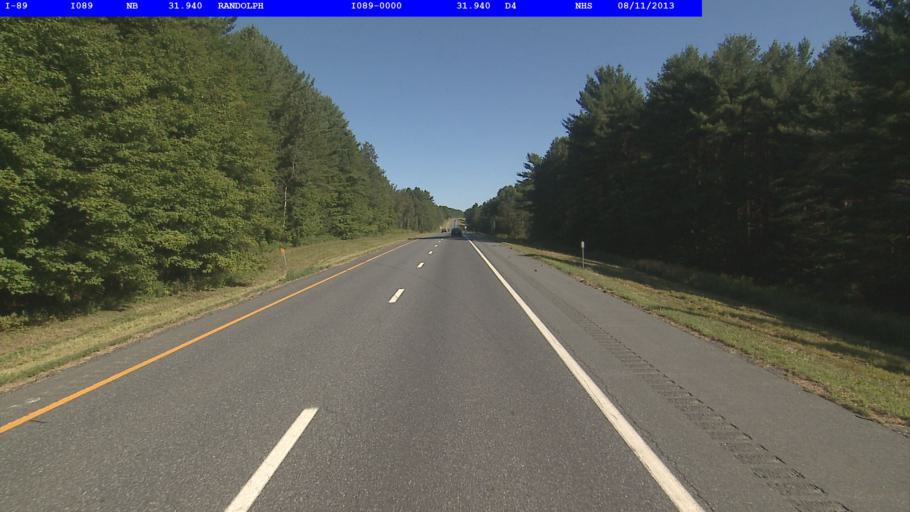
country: US
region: Vermont
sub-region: Orange County
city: Randolph
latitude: 43.9595
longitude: -72.6228
